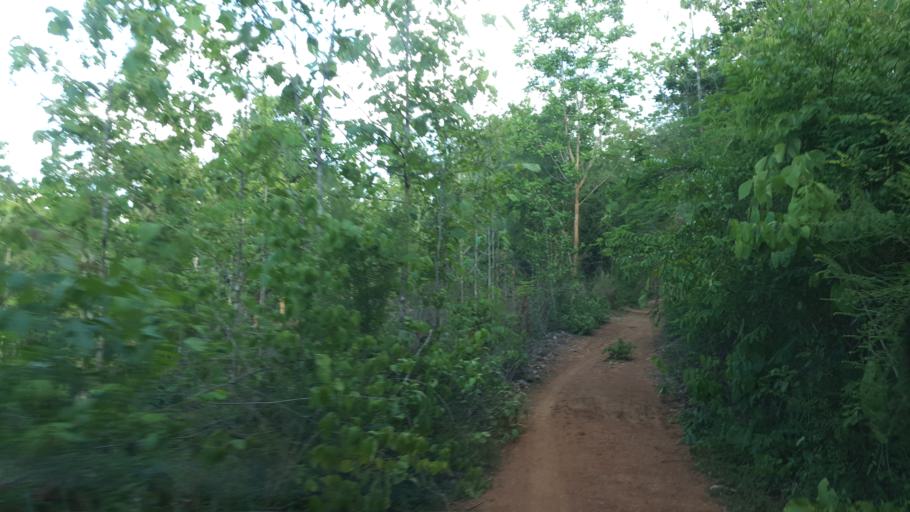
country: TH
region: Lampang
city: Sop Prap
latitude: 17.8912
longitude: 99.2866
